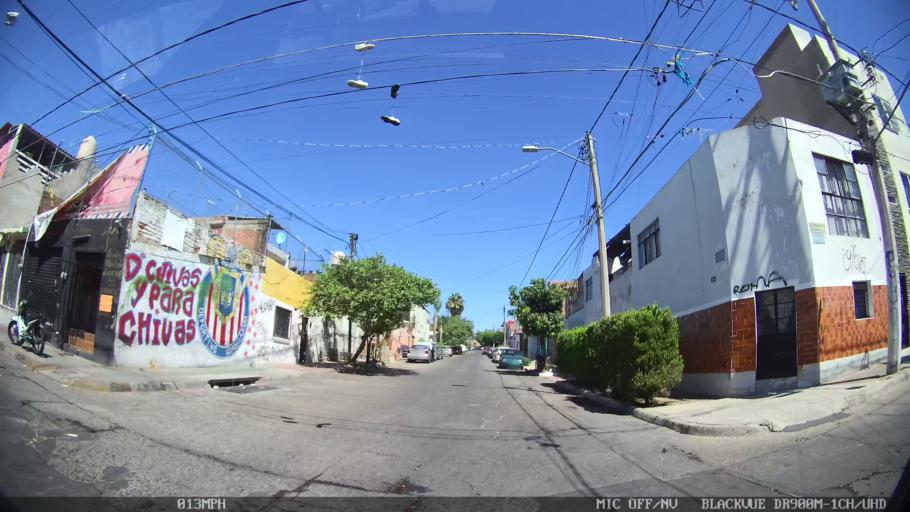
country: MX
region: Jalisco
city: Tlaquepaque
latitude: 20.6970
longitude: -103.2925
